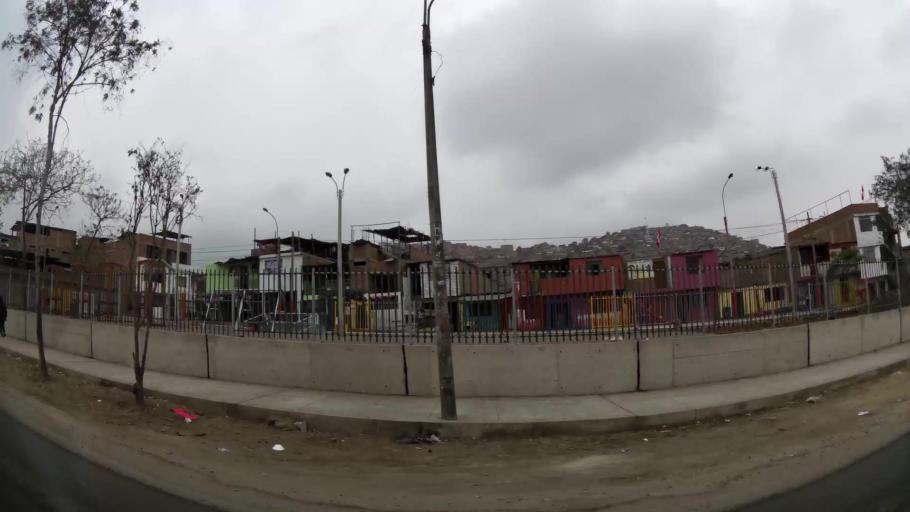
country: PE
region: Lima
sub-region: Lima
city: Surco
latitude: -12.1426
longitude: -76.9641
